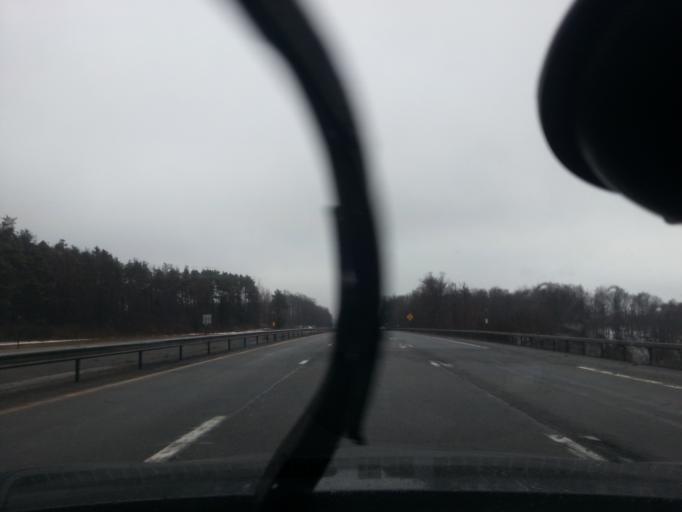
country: US
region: New York
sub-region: Onondaga County
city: Nedrow
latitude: 42.9227
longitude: -76.1225
